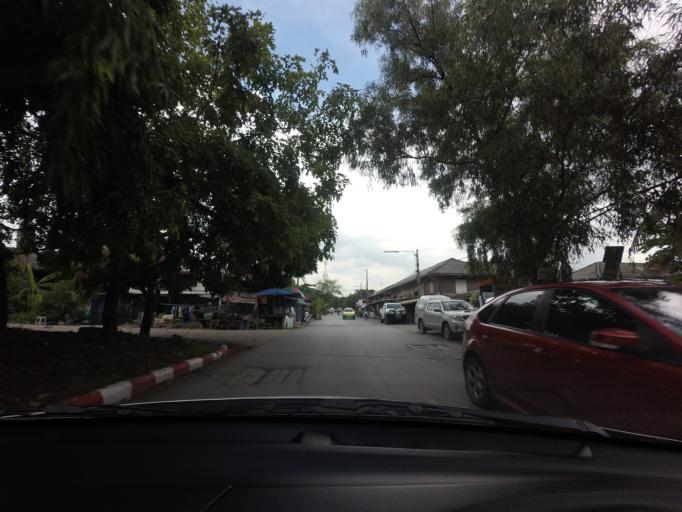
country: TH
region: Bangkok
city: Chatuchak
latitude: 13.8209
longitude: 100.5514
